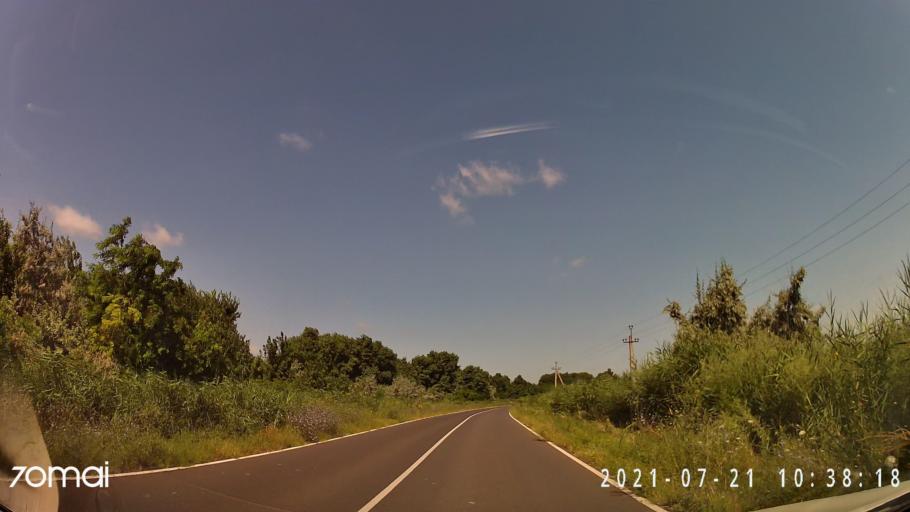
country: RO
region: Tulcea
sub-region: Oras Isaccea
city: Isaccea
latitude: 45.2968
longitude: 28.4410
